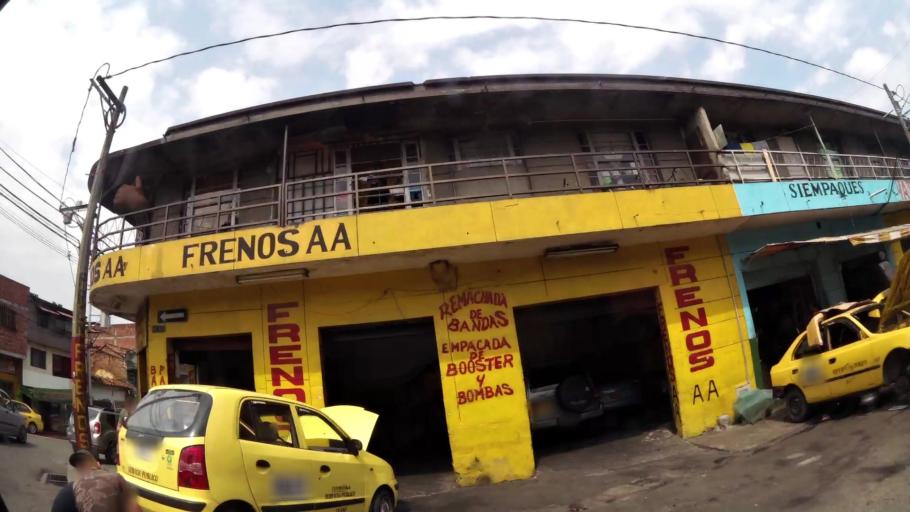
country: CO
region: Antioquia
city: Medellin
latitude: 6.2669
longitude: -75.5599
